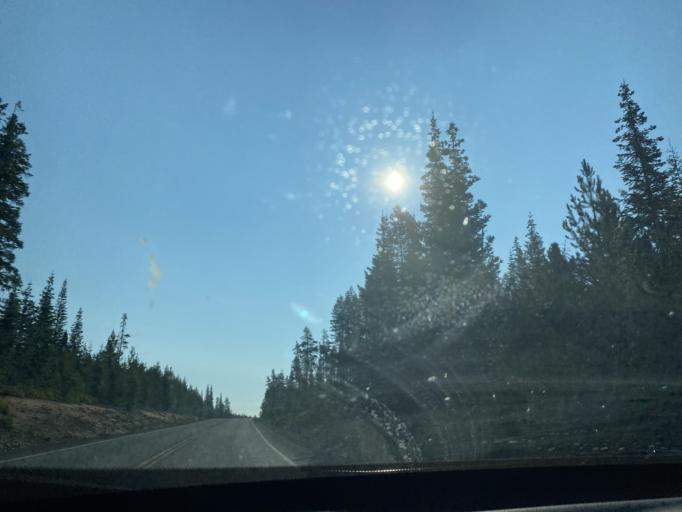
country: US
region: Oregon
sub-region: Deschutes County
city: La Pine
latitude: 43.7038
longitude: -121.3126
